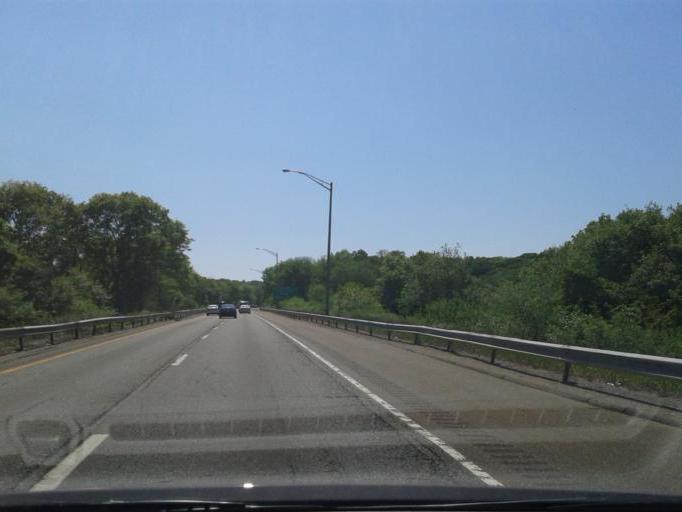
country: US
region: Connecticut
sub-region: New London County
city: Mystic
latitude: 41.3732
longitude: -71.9670
